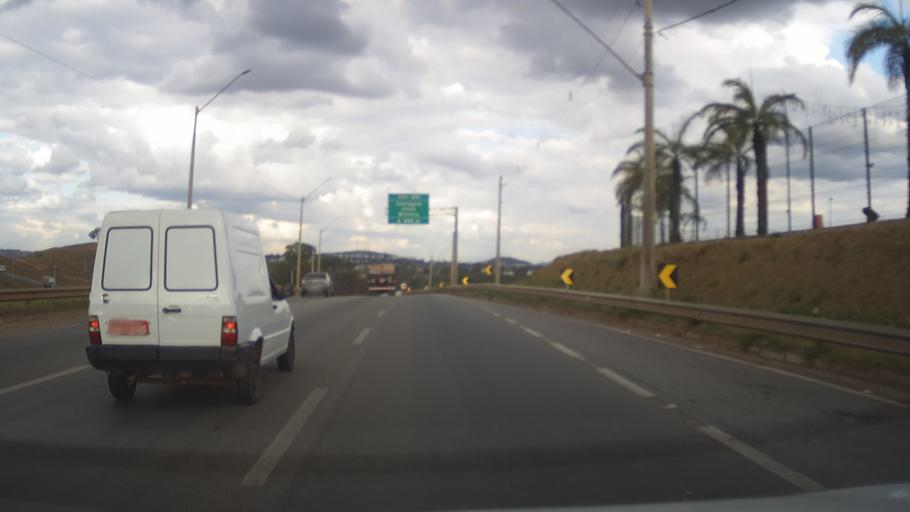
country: BR
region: Minas Gerais
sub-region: Betim
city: Betim
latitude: -19.9617
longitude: -44.1579
